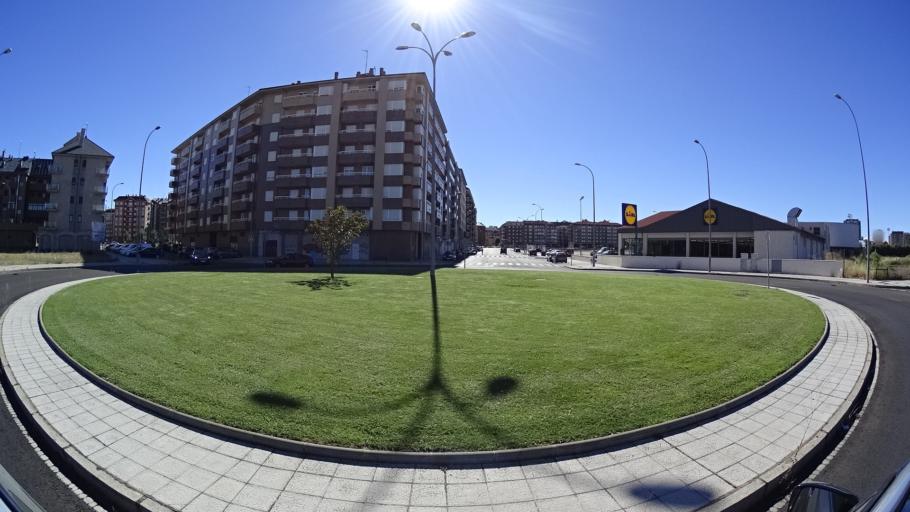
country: ES
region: Castille and Leon
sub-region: Provincia de Leon
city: Leon
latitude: 42.6059
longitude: -5.5592
